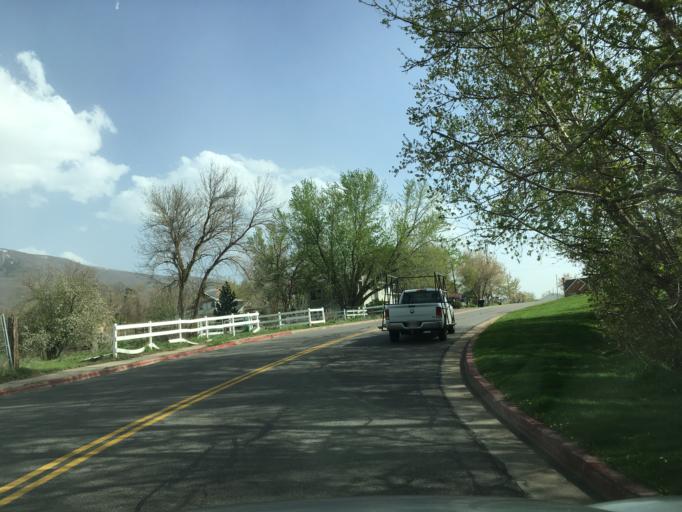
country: US
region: Utah
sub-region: Davis County
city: Farmington
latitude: 40.9818
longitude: -111.8964
